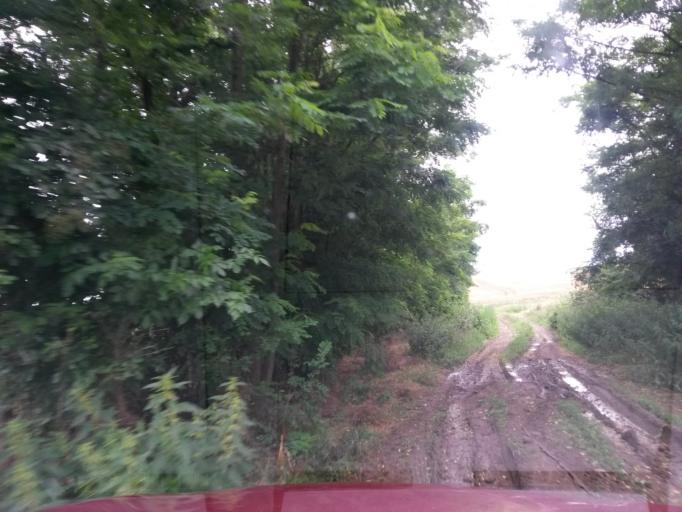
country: SK
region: Banskobystricky
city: Dudince
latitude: 48.1301
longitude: 18.8574
